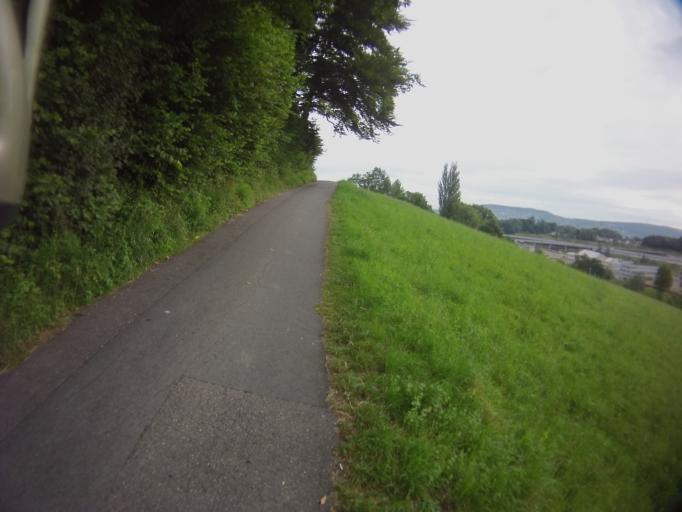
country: CH
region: Zurich
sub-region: Bezirk Zuerich
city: Zuerich (Kreis 2) / Unter-Leimbach
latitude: 47.3374
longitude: 8.5142
